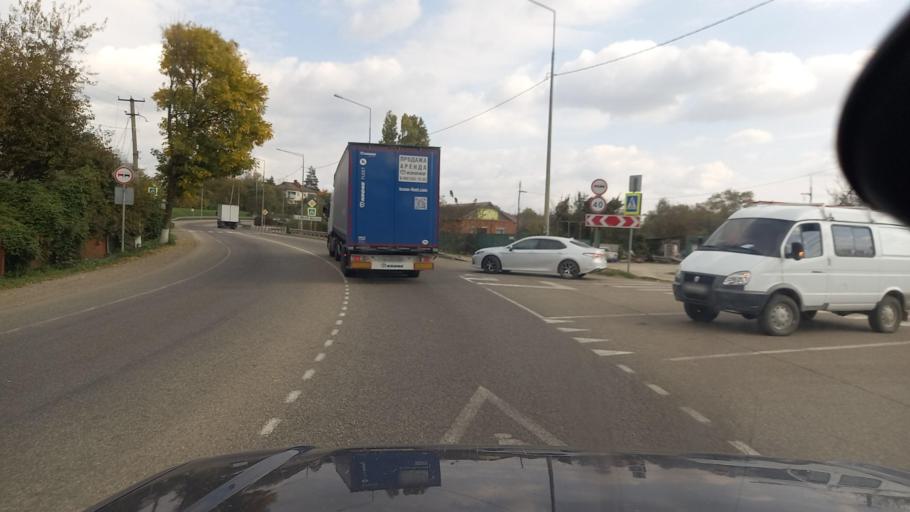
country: RU
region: Krasnodarskiy
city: Kholmskiy
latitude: 44.8493
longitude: 38.3986
